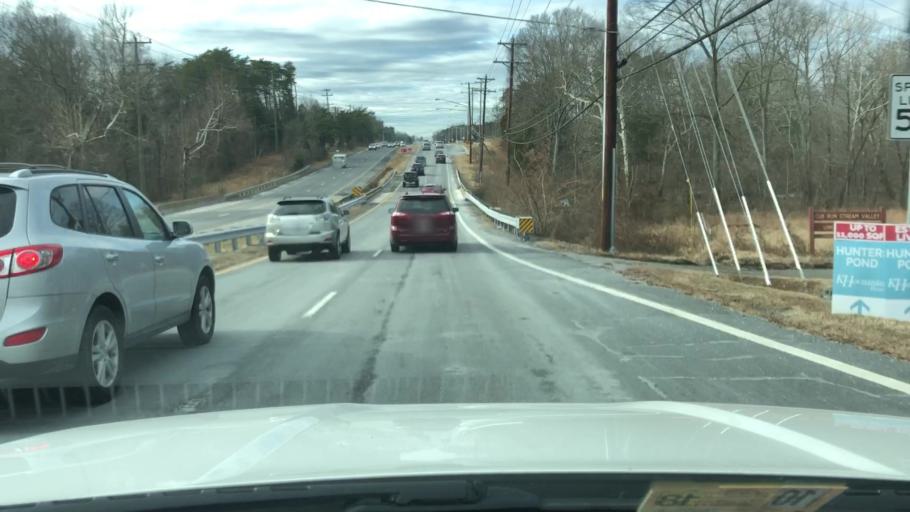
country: US
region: Virginia
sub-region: Fairfax County
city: Centreville
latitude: 38.8335
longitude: -77.4628
